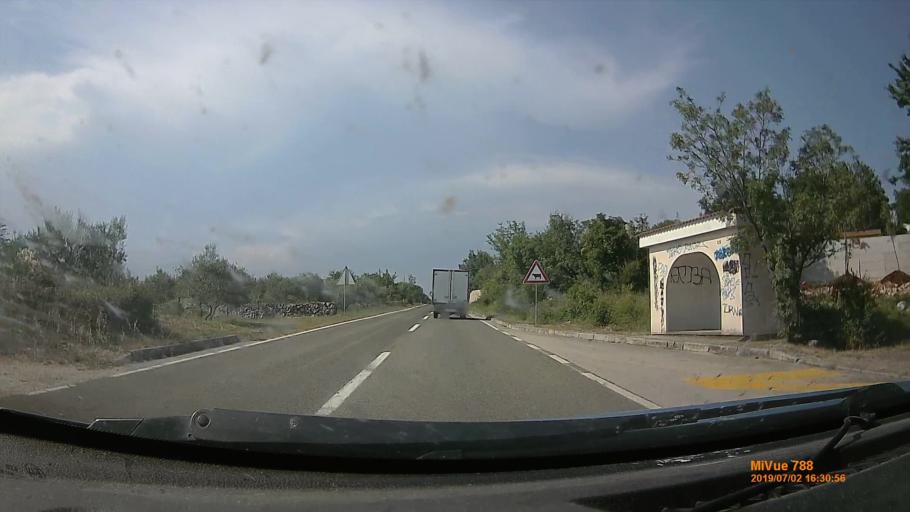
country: HR
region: Primorsko-Goranska
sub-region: Grad Krk
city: Krk
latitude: 45.0482
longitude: 14.4887
